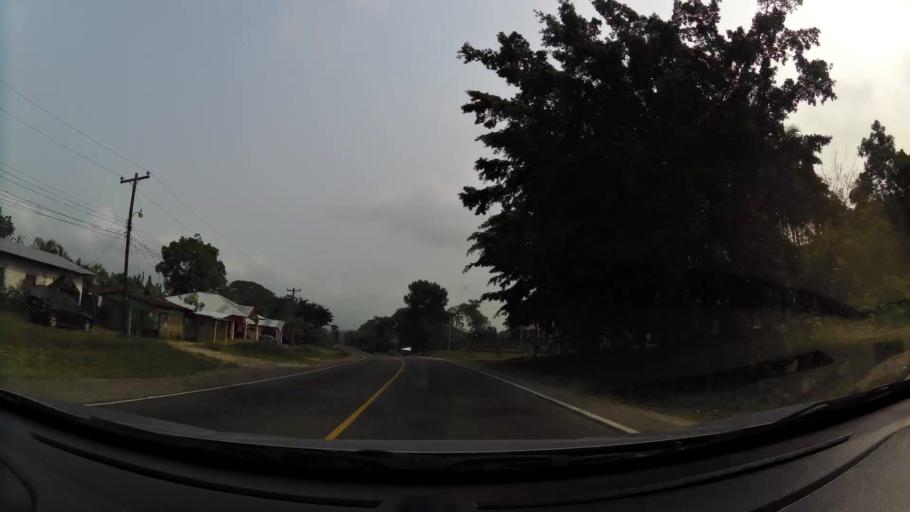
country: HN
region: Atlantida
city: Mezapa
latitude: 15.5954
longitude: -87.6084
